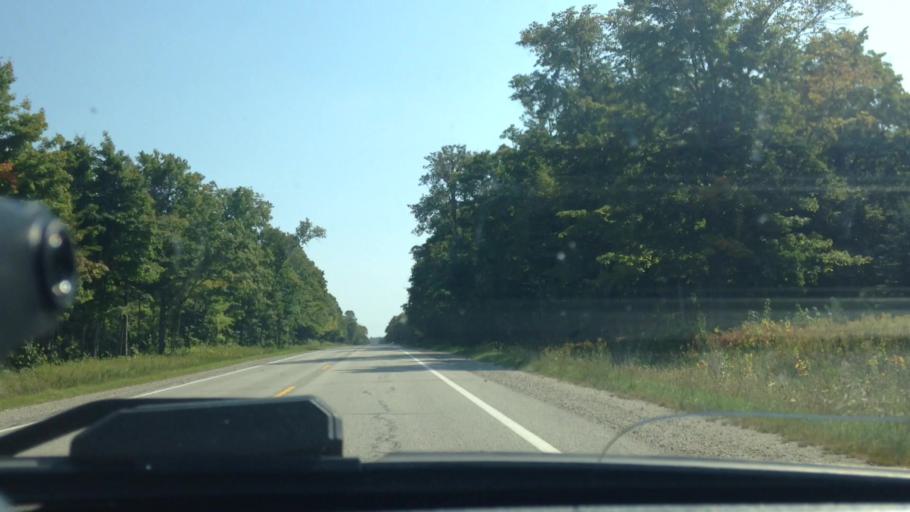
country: US
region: Michigan
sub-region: Luce County
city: Newberry
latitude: 46.3233
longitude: -85.6697
